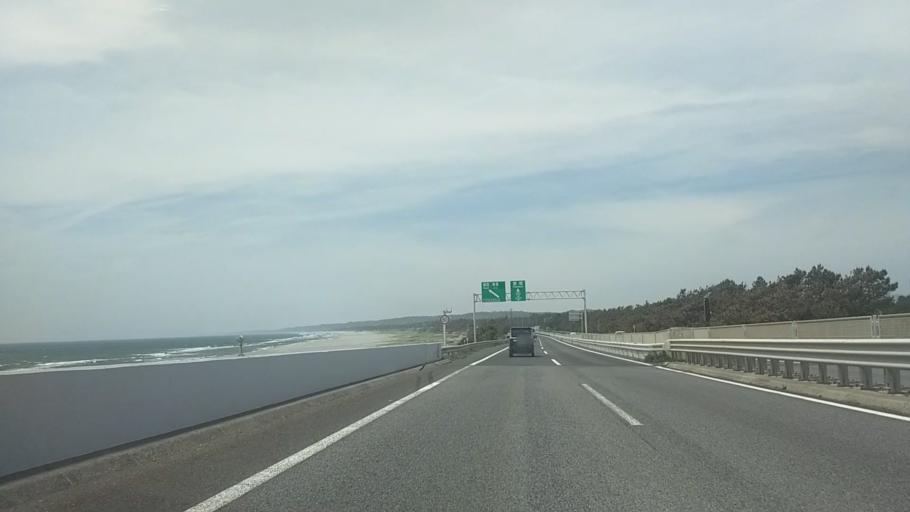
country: JP
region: Shizuoka
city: Kosai-shi
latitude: 34.6795
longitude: 137.5898
